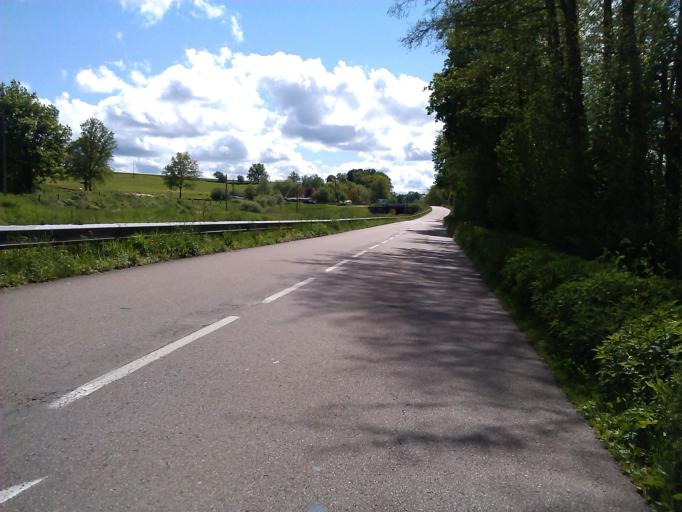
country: FR
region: Bourgogne
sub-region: Departement de Saone-et-Loire
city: Ecuisses
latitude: 46.7835
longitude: 4.5526
